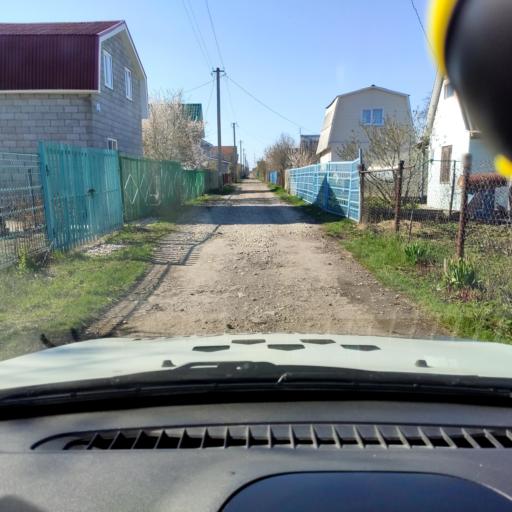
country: RU
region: Samara
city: Tol'yatti
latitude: 53.5987
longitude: 49.2951
